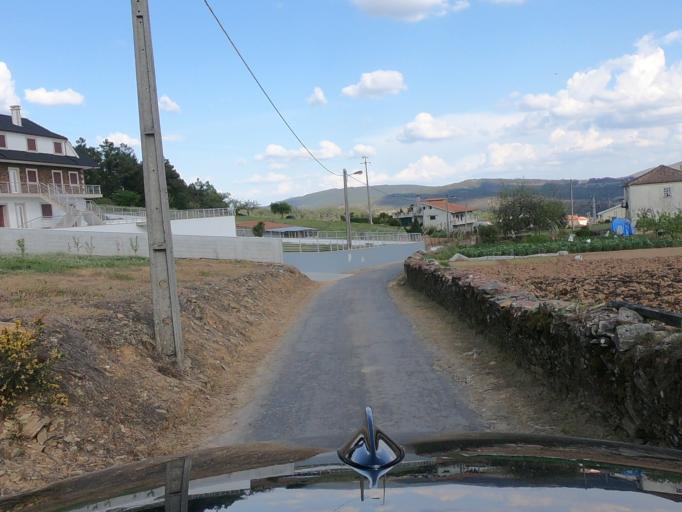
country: PT
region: Vila Real
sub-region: Sabrosa
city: Vilela
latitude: 41.2431
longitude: -7.6579
